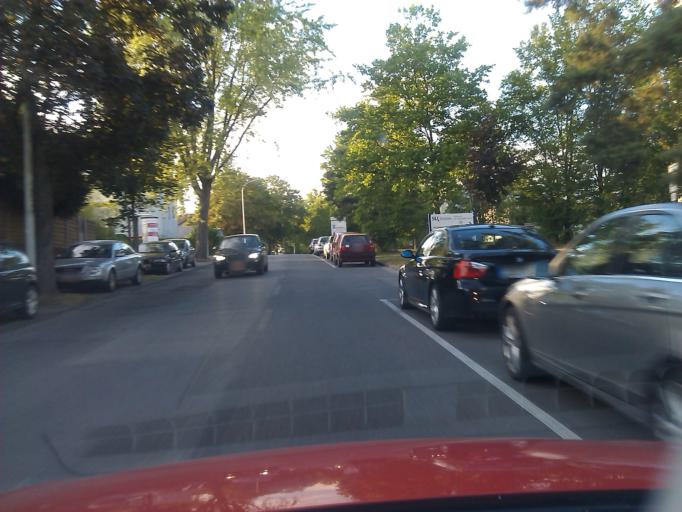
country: DE
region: Baden-Wuerttemberg
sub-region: Regierungsbezirk Stuttgart
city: Heilbronn
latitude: 49.1523
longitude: 9.1875
